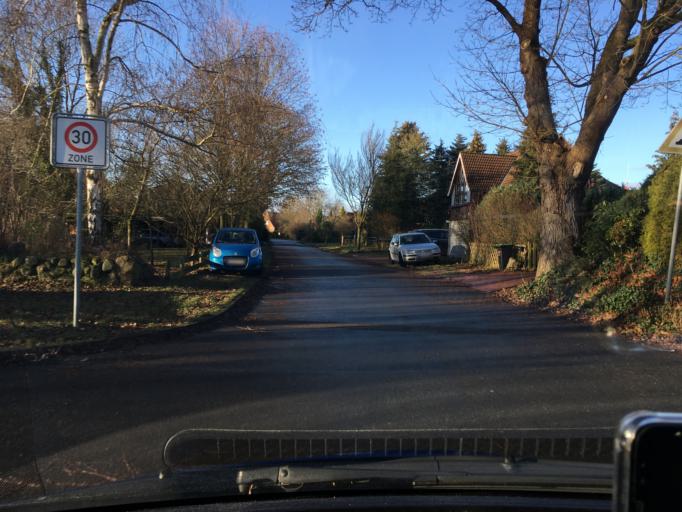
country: DE
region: Lower Saxony
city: Wendisch Evern
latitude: 53.2181
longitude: 10.4690
